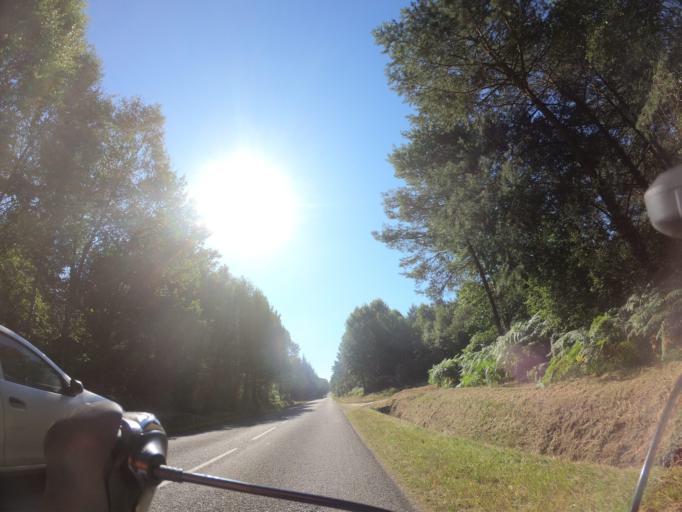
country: FR
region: Lower Normandy
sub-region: Departement de l'Orne
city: Juvigny-sous-Andaine
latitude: 48.5828
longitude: -0.4779
